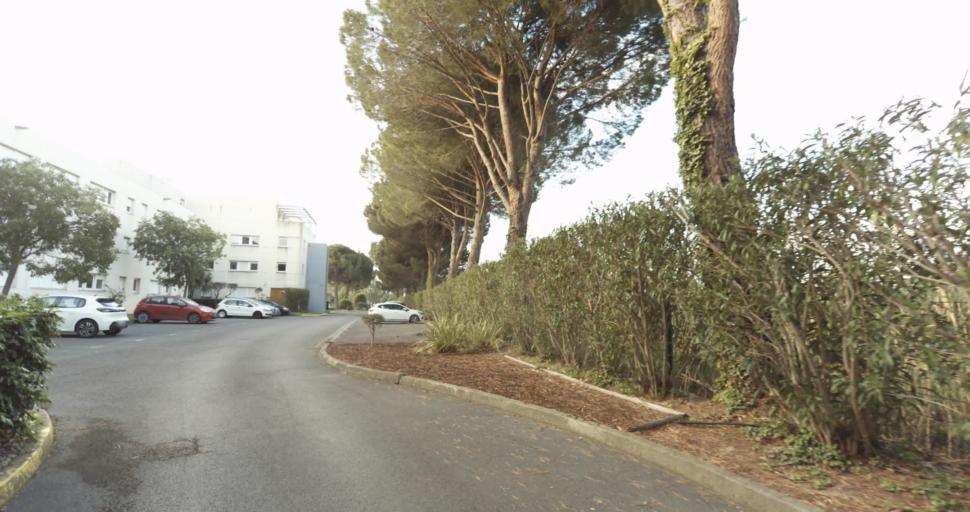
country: FR
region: Languedoc-Roussillon
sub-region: Departement du Gard
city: Caissargues
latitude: 43.8236
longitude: 4.3854
